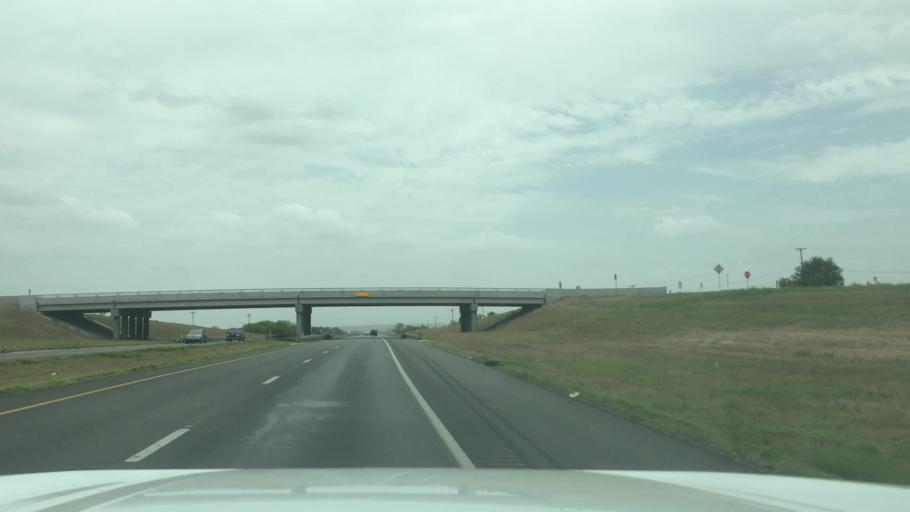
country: US
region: Texas
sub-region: McLennan County
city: Woodway
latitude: 31.5738
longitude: -97.2889
